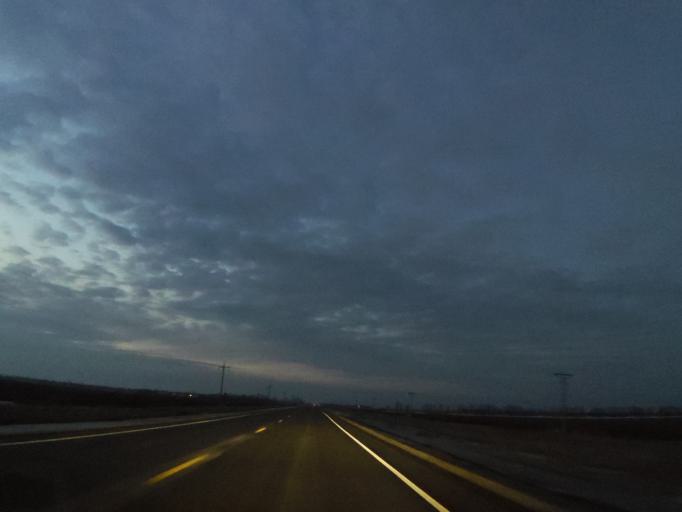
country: US
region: North Dakota
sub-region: Walsh County
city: Park River
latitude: 48.2551
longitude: -97.6225
